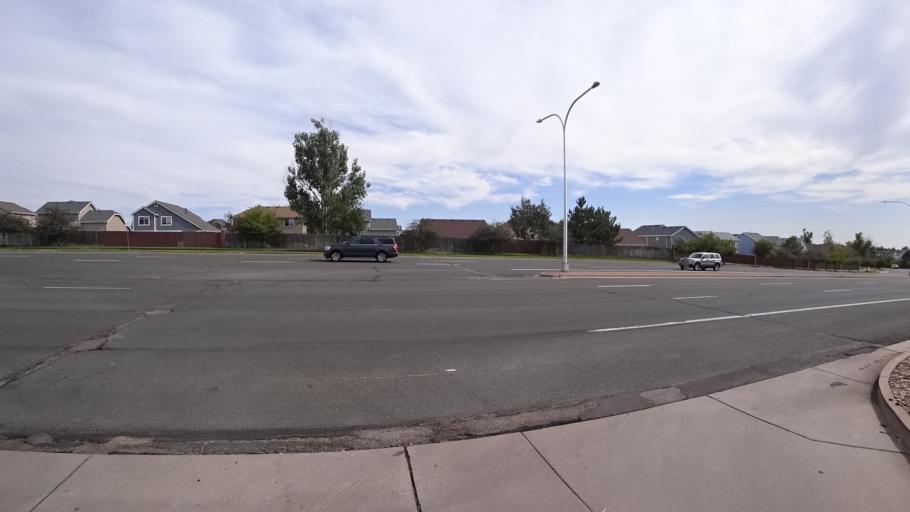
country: US
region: Colorado
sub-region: El Paso County
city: Cimarron Hills
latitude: 38.9098
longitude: -104.6956
